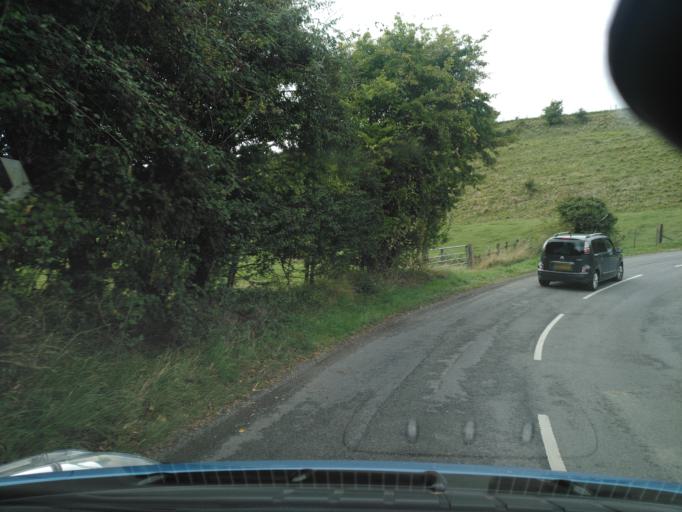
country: GB
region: England
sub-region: Oxfordshire
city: Stanford in the Vale
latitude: 51.5823
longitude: -1.5481
